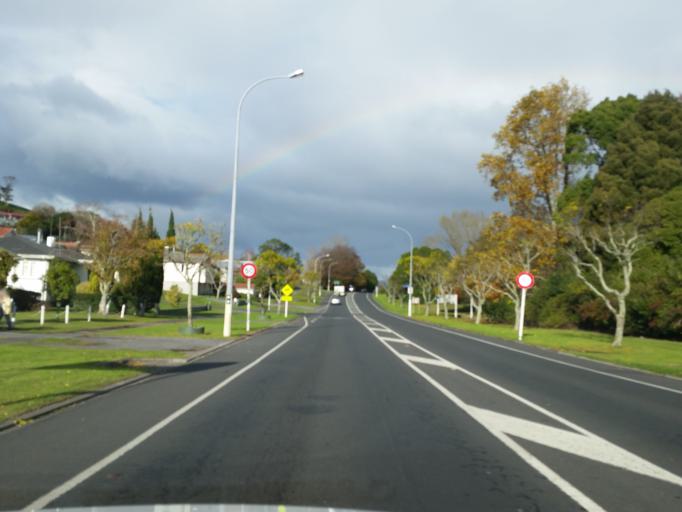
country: NZ
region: Waikato
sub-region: Hauraki District
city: Paeroa
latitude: -37.3844
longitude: 175.6766
